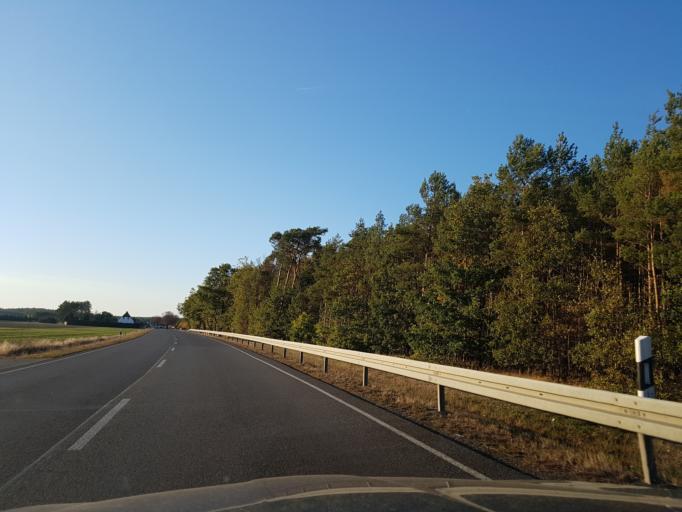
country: DE
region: Brandenburg
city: Bad Liebenwerda
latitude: 51.5435
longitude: 13.3931
